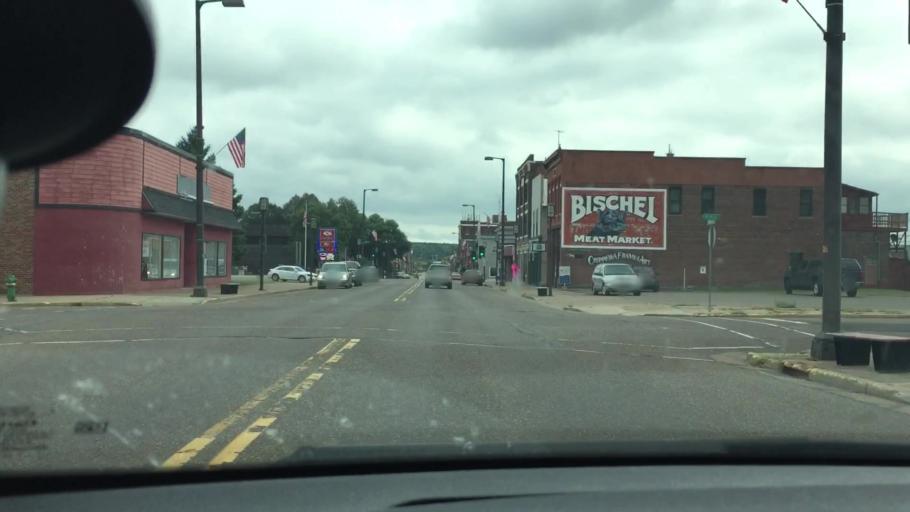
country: US
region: Wisconsin
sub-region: Chippewa County
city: Chippewa Falls
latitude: 44.9389
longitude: -91.3957
